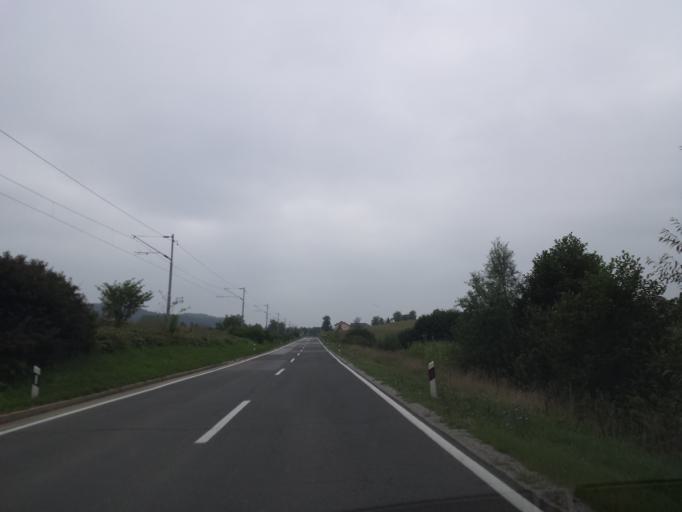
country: HR
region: Karlovacka
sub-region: Grad Karlovac
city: Karlovac
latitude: 45.4316
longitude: 15.4897
